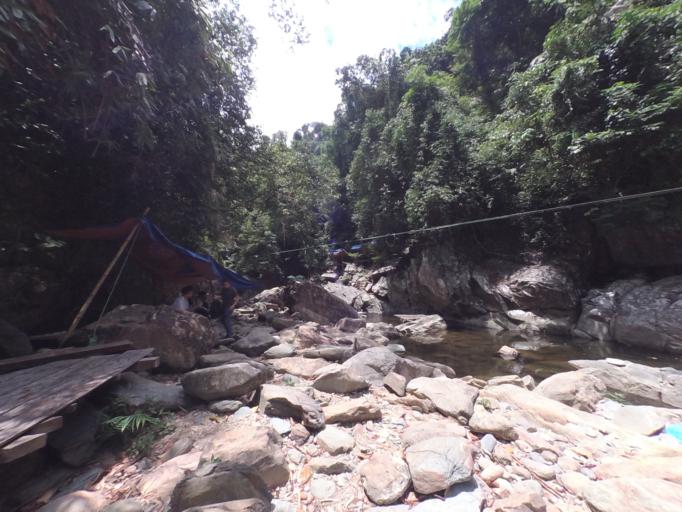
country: VN
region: Thua Thien-Hue
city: A Luoi
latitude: 16.3071
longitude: 107.3239
